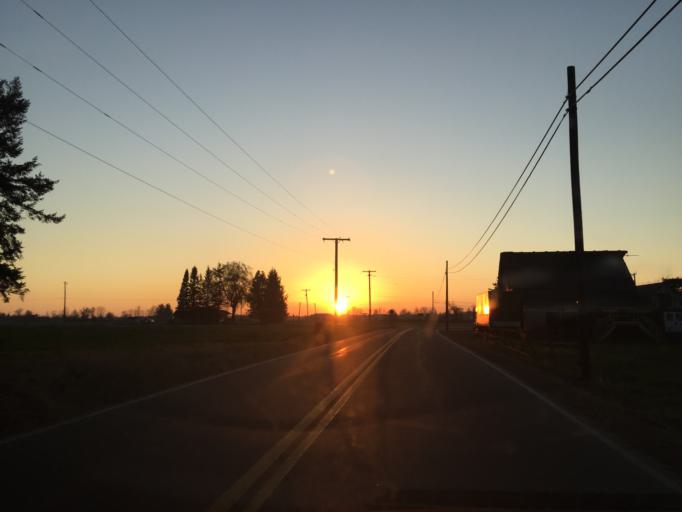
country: US
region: Washington
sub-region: Whatcom County
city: Sumas
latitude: 48.9855
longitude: -122.2458
